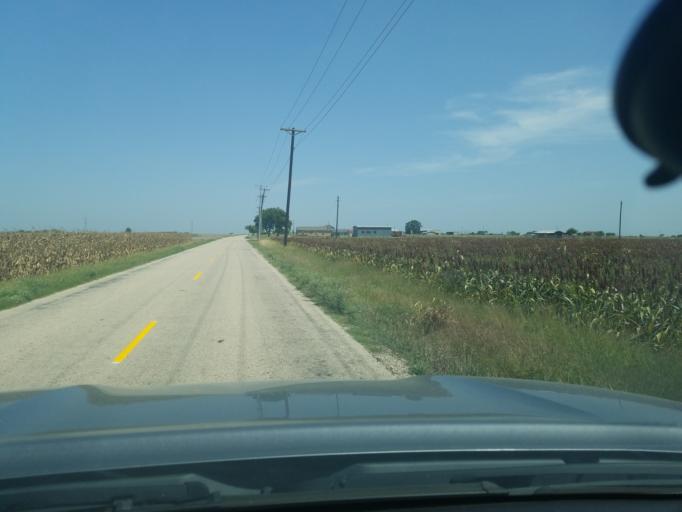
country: US
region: Texas
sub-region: Guadalupe County
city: Lake Dunlap
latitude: 29.6828
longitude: -98.0308
